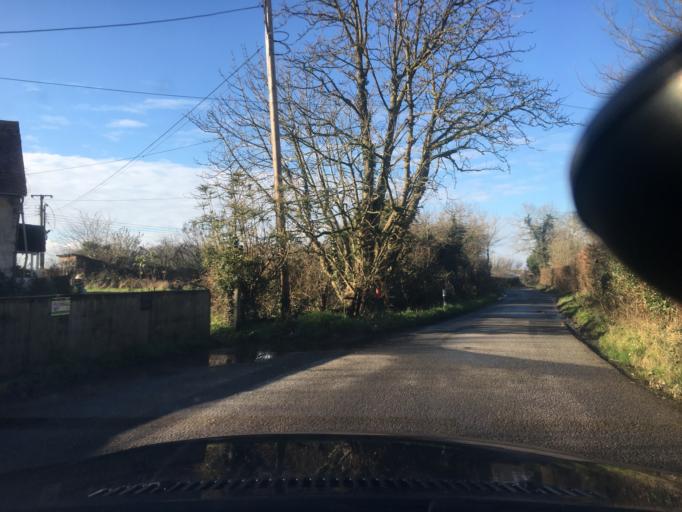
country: GB
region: England
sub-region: West Berkshire
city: Stratfield Mortimer
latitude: 51.3932
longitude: -1.0231
